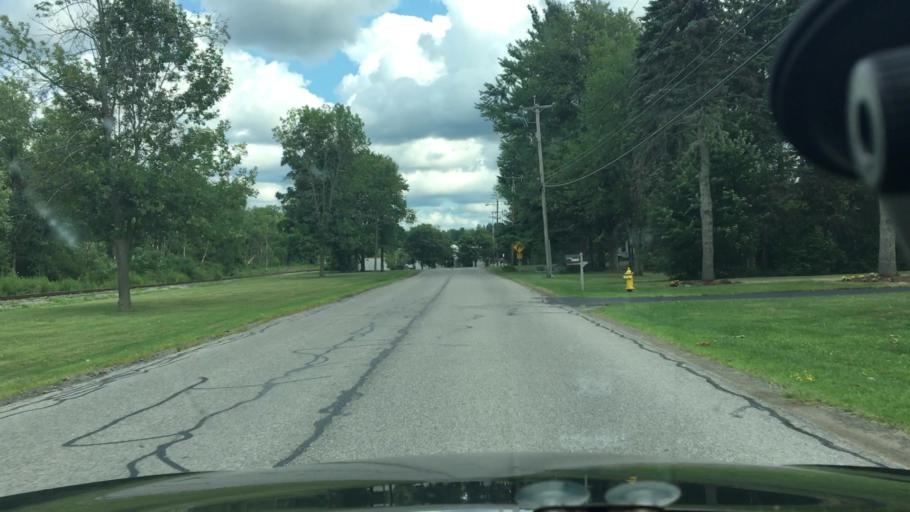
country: US
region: New York
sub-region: Erie County
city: Orchard Park
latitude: 42.7680
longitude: -78.7628
